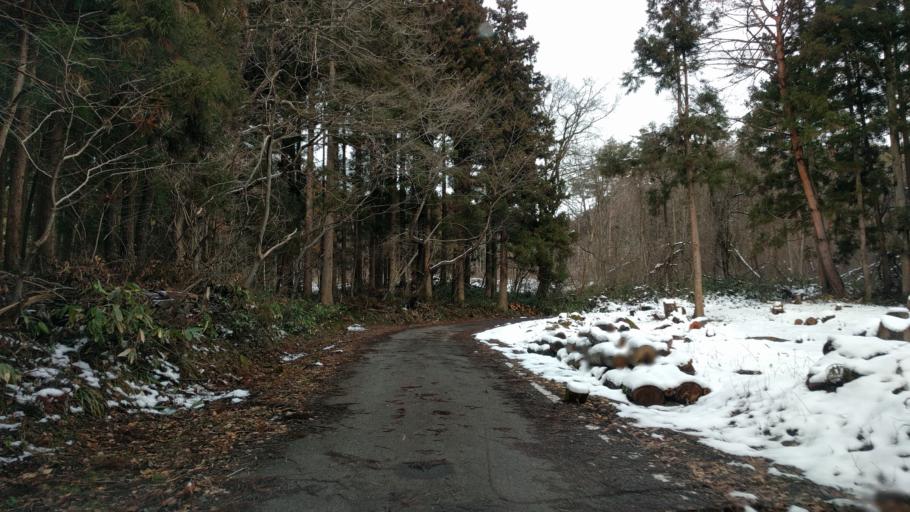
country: JP
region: Fukushima
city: Inawashiro
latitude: 37.5732
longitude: 139.9941
